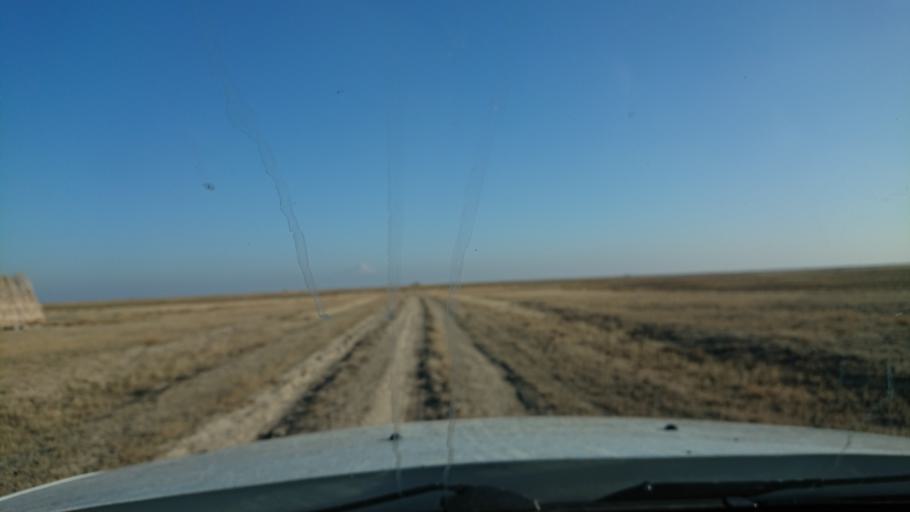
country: TR
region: Aksaray
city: Sultanhani
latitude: 38.3942
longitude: 33.5927
